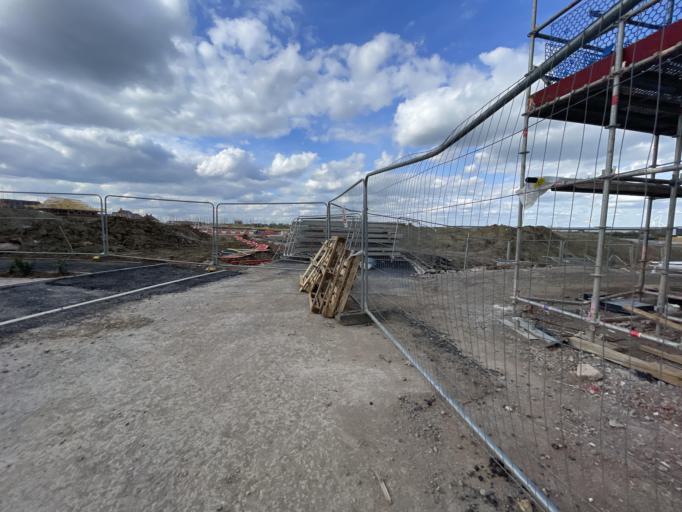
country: GB
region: England
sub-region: Warwickshire
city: Rugby
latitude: 52.3612
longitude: -1.1826
